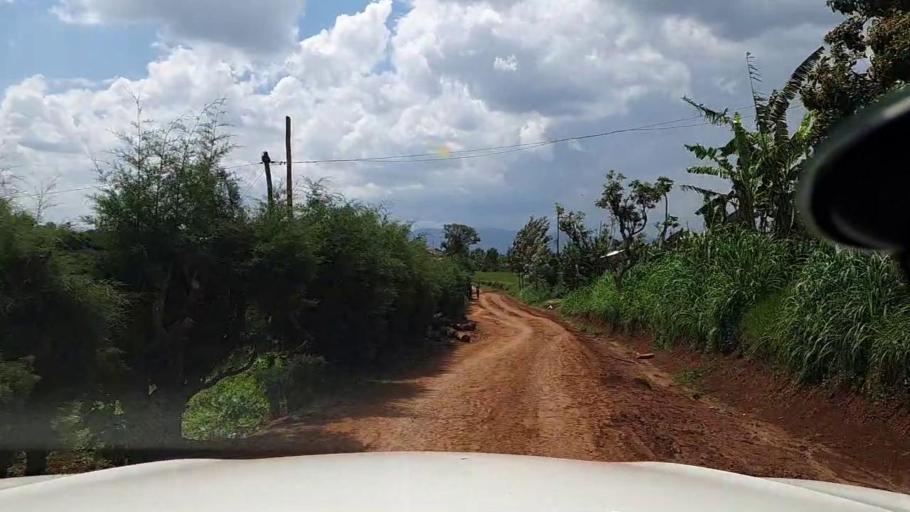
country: RW
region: Kigali
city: Kigali
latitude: -1.8331
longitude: 29.8392
